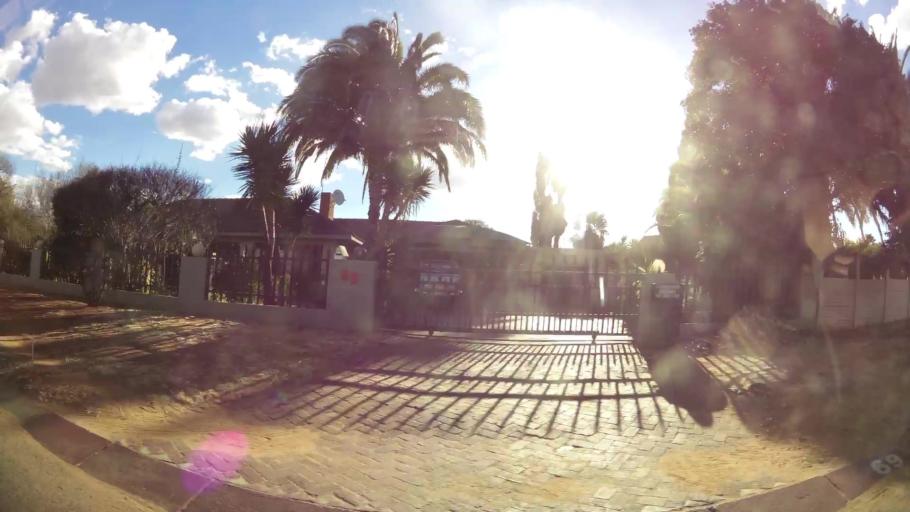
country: ZA
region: North-West
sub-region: Dr Kenneth Kaunda District Municipality
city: Klerksdorp
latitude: -26.8406
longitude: 26.6576
